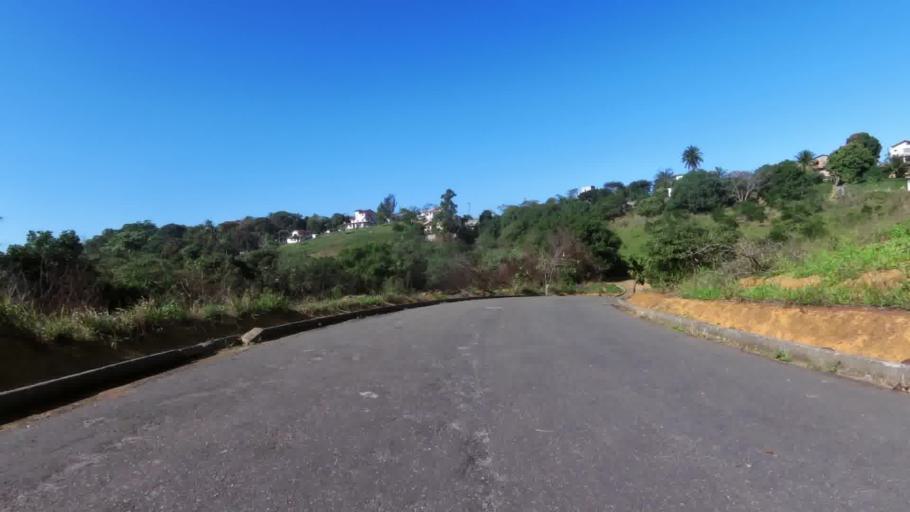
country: BR
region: Espirito Santo
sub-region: Guarapari
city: Guarapari
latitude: -20.7384
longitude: -40.5597
